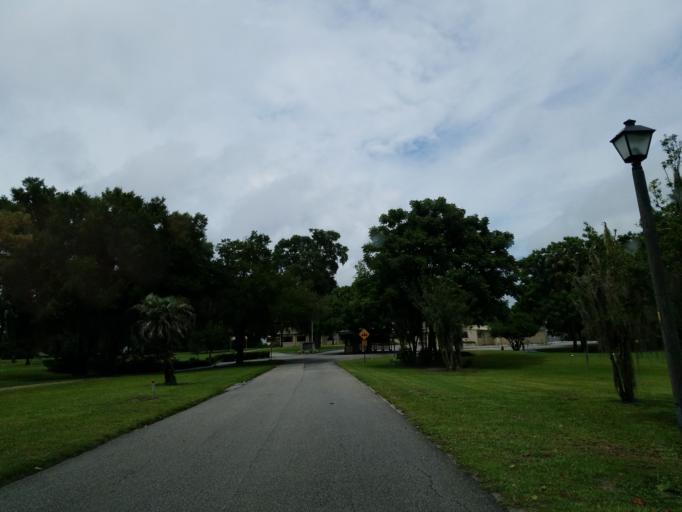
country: US
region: Florida
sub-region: Citrus County
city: Inverness
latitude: 28.8154
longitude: -82.2897
